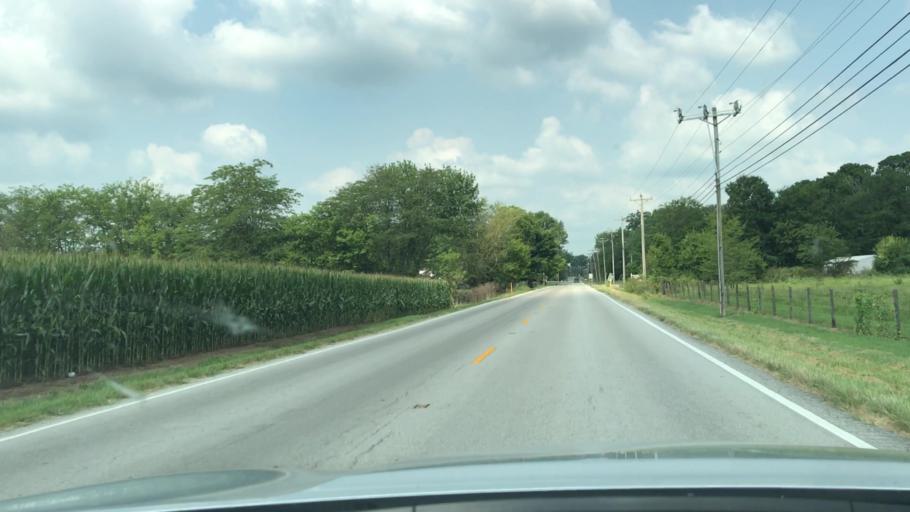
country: US
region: Kentucky
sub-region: Todd County
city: Elkton
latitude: 36.8072
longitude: -87.1389
